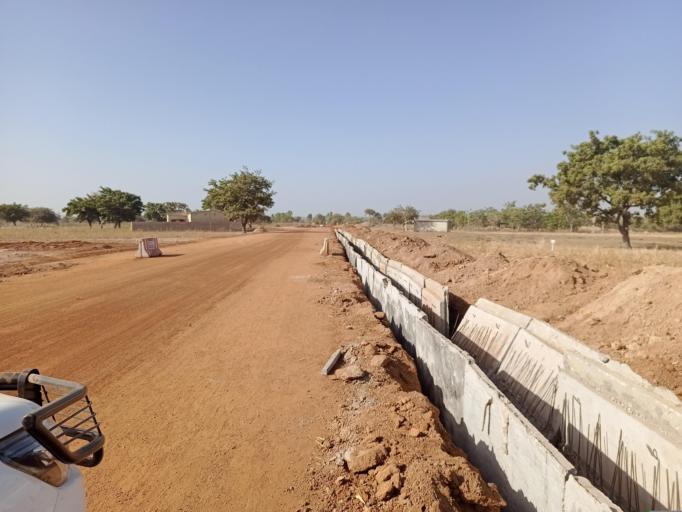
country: BF
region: Centre-Est
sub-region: Province du Boulgou
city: Garango
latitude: 11.4777
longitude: -0.5340
